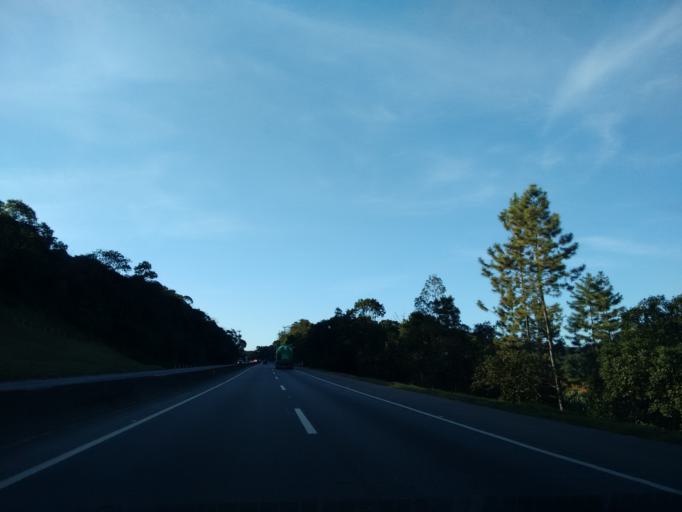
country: BR
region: Santa Catarina
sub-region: Joinville
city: Joinville
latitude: -26.0921
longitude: -48.8645
